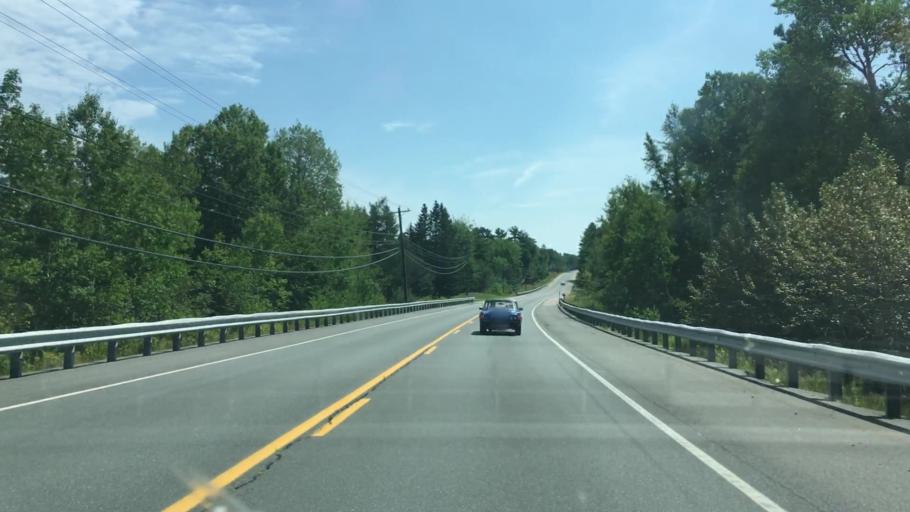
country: US
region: Maine
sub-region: Washington County
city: Calais
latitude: 45.1647
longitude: -67.2075
